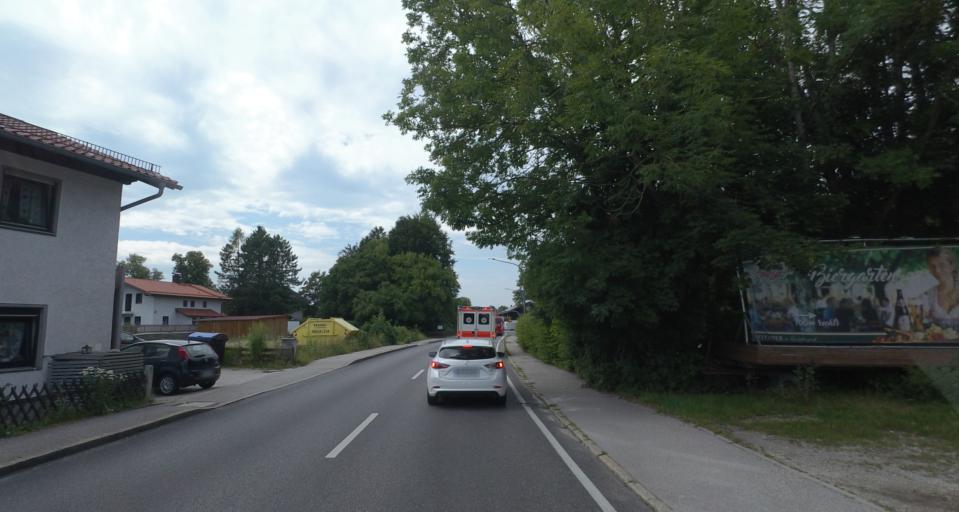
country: DE
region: Bavaria
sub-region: Upper Bavaria
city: Trostberg an der Alz
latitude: 47.9853
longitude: 12.5485
